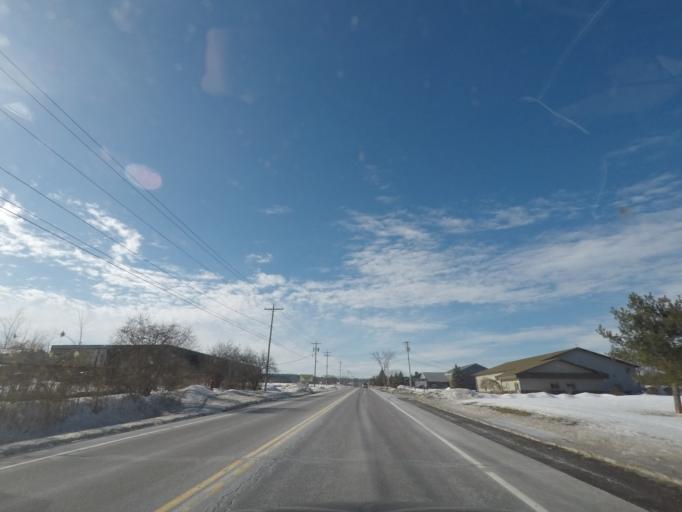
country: US
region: New York
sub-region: Albany County
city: Altamont
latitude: 42.7486
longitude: -74.0425
